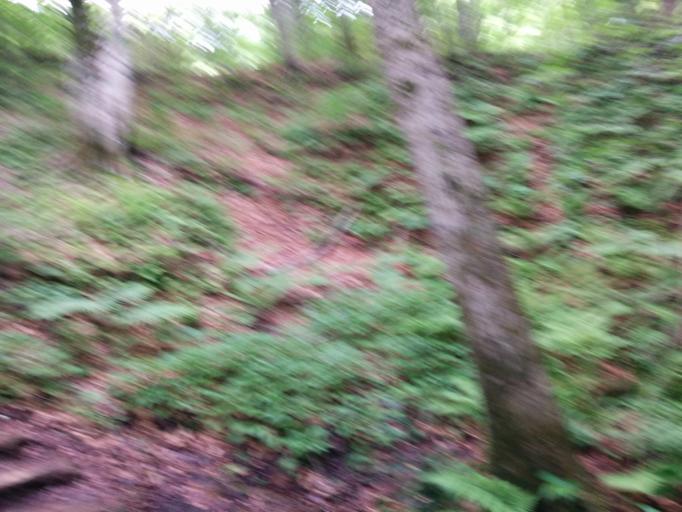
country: JP
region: Aomori
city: Hirosaki
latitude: 40.5197
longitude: 140.1687
